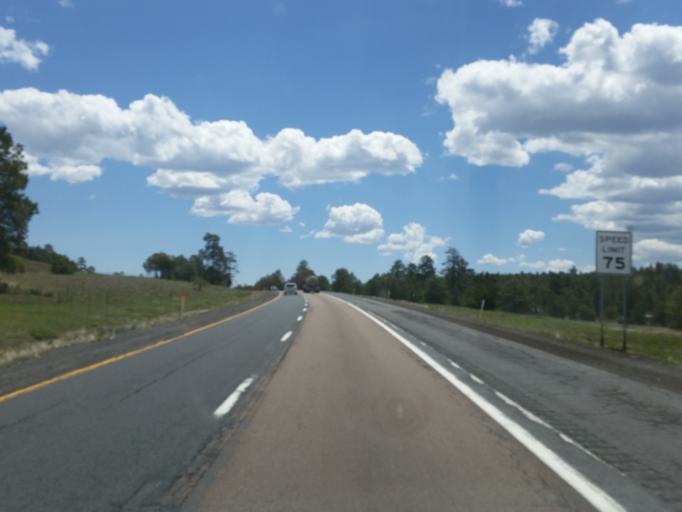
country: US
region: Arizona
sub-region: Coconino County
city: Flagstaff
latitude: 35.1996
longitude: -111.7549
